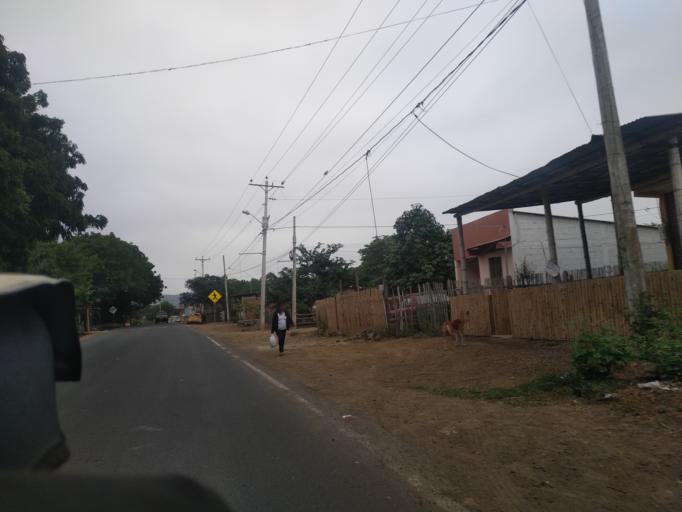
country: EC
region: Manabi
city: Montecristi
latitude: -1.0752
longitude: -80.6681
